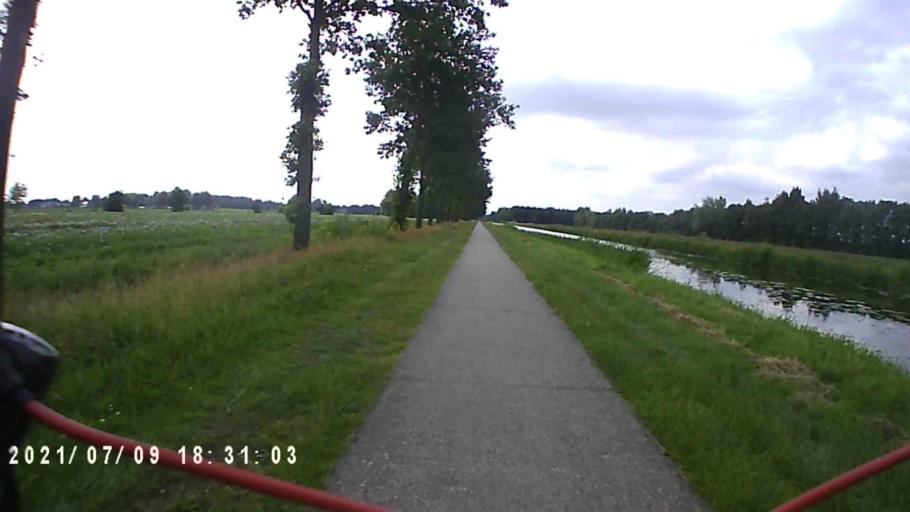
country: NL
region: Groningen
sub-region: Gemeente Pekela
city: Oude Pekela
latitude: 53.0671
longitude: 6.9749
